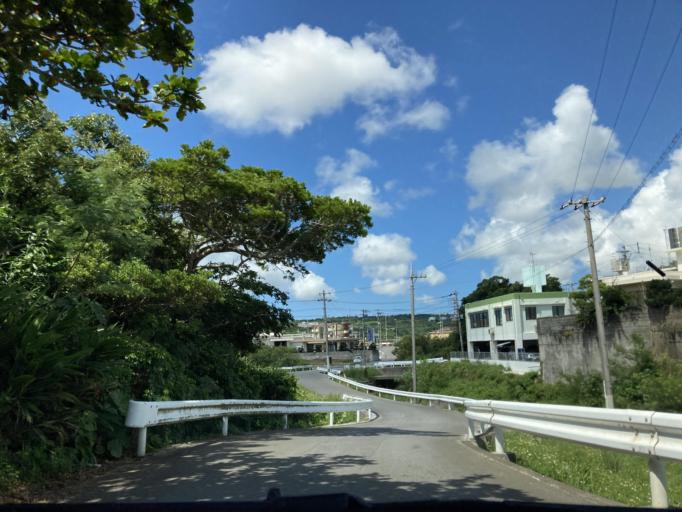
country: JP
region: Okinawa
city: Itoman
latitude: 26.1203
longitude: 127.7439
